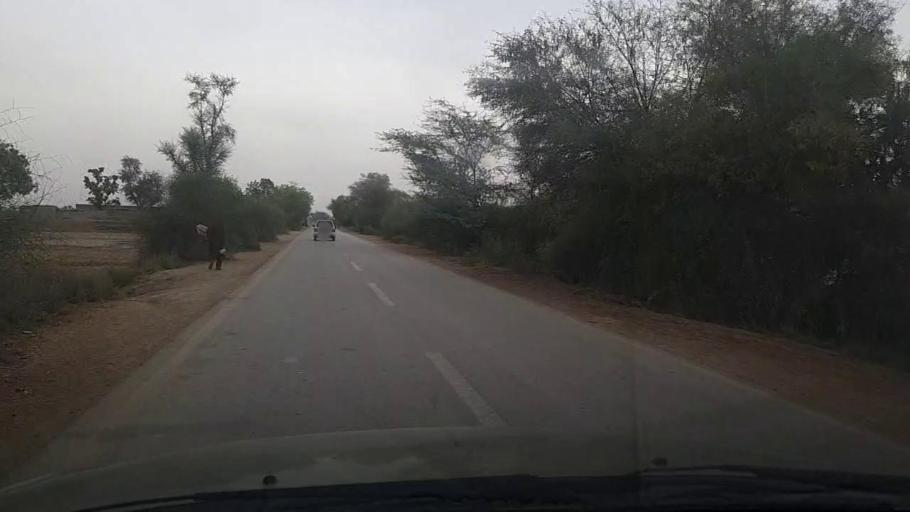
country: PK
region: Sindh
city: Daulatpur
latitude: 26.3286
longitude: 68.1118
